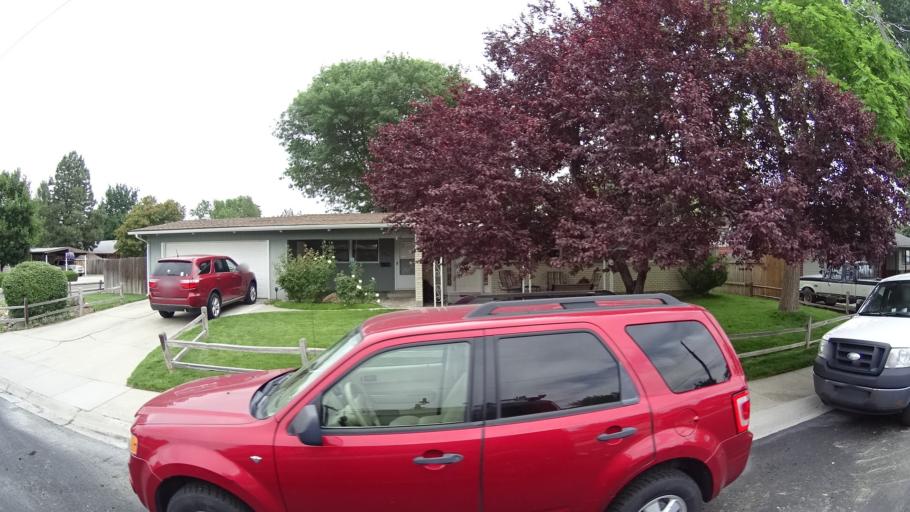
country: US
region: Idaho
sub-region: Ada County
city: Boise
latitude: 43.5769
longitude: -116.2037
